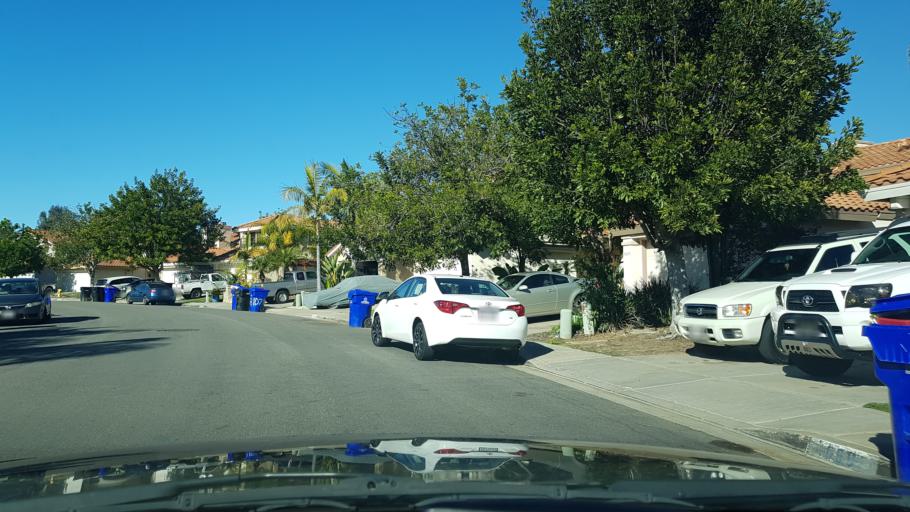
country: US
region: California
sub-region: San Diego County
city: Fairbanks Ranch
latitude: 32.9117
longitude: -117.1665
